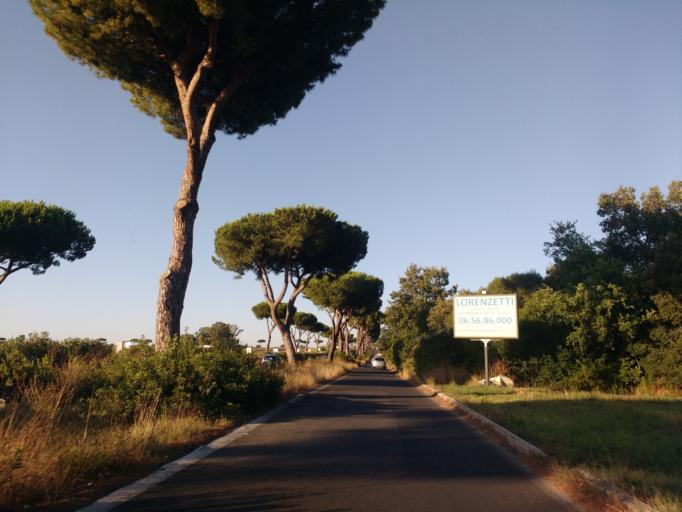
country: IT
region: Latium
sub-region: Citta metropolitana di Roma Capitale
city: Acilia-Castel Fusano-Ostia Antica
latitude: 41.7593
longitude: 12.3758
